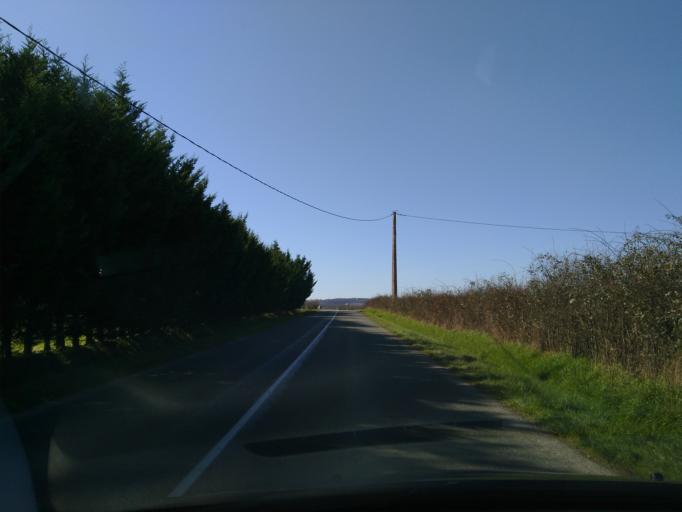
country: FR
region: Aquitaine
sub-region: Departement du Lot-et-Garonne
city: Saint-Hilaire
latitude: 44.5375
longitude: 0.6740
